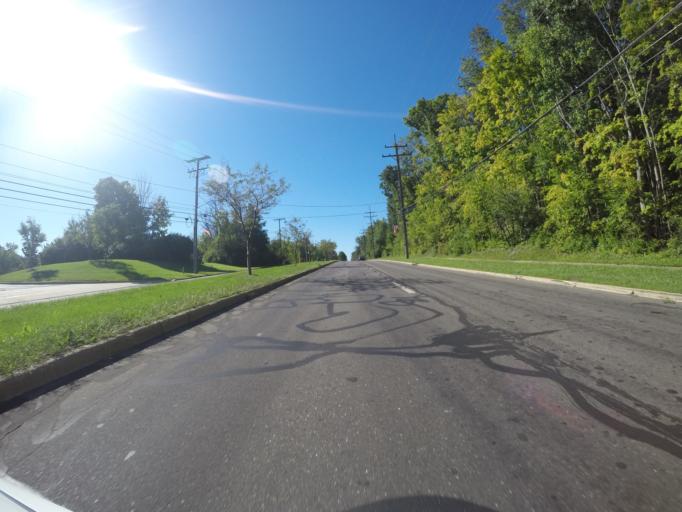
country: US
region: Ohio
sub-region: Cuyahoga County
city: Brecksville
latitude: 41.3119
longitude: -81.6270
